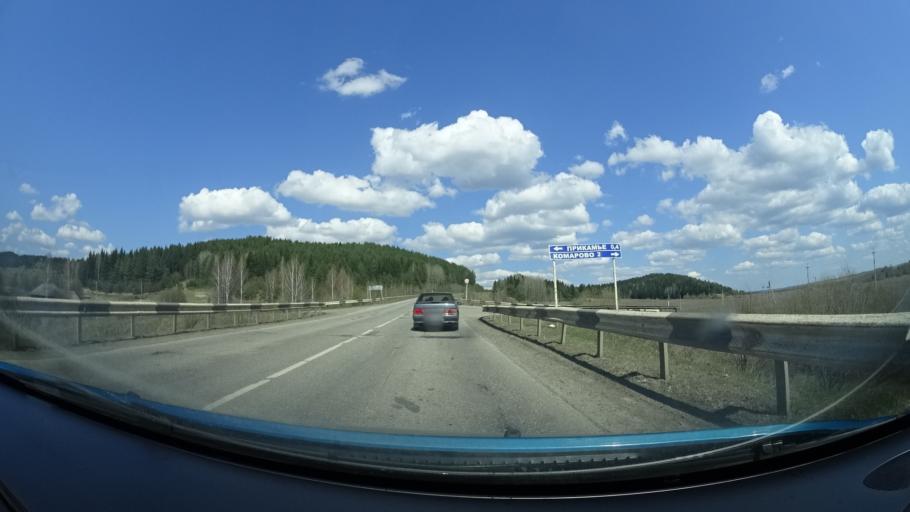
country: RU
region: Perm
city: Osa
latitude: 57.3015
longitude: 55.6157
